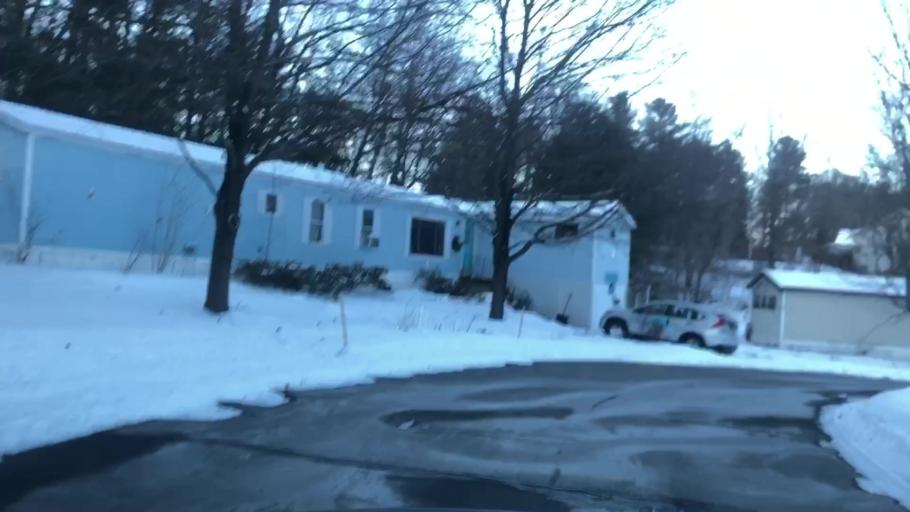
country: US
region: New Hampshire
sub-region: Hillsborough County
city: Milford
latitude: 42.8143
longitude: -71.6678
